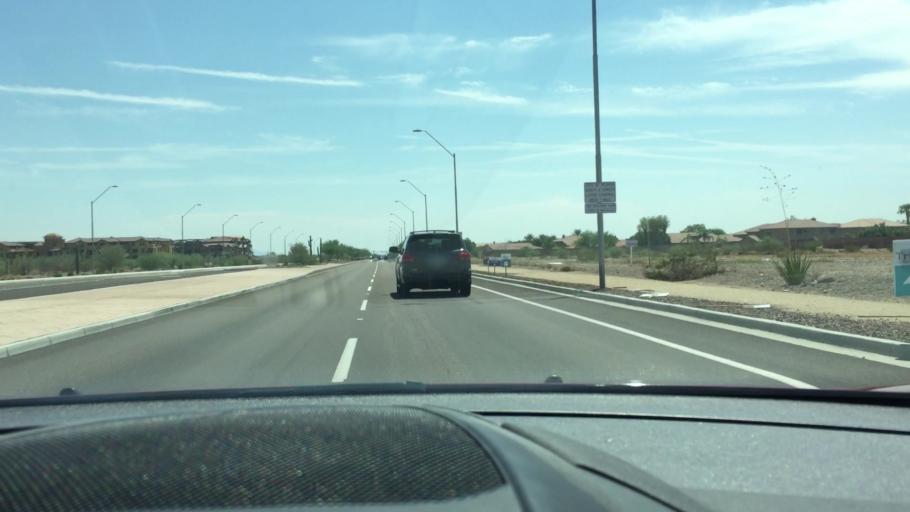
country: US
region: Arizona
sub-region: Maricopa County
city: Sun City West
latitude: 33.7381
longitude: -112.2630
